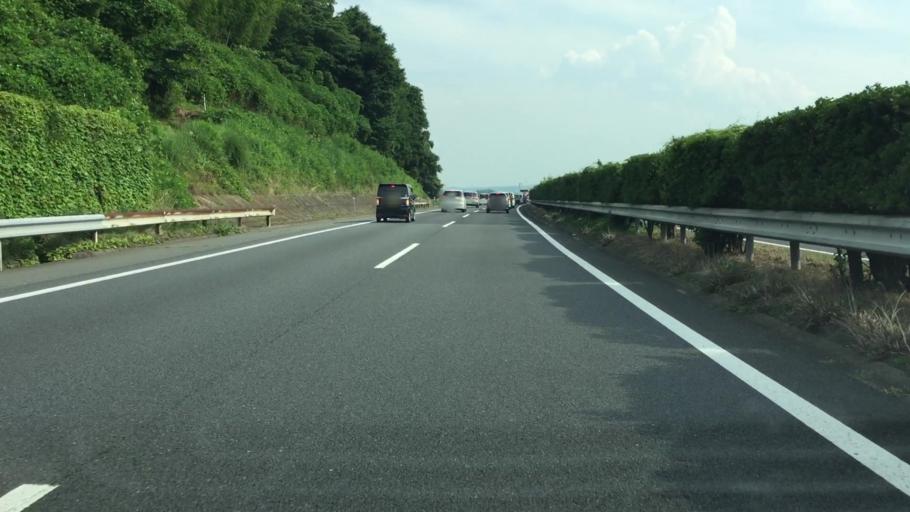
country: JP
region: Tochigi
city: Yaita
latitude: 36.8595
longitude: 139.9133
